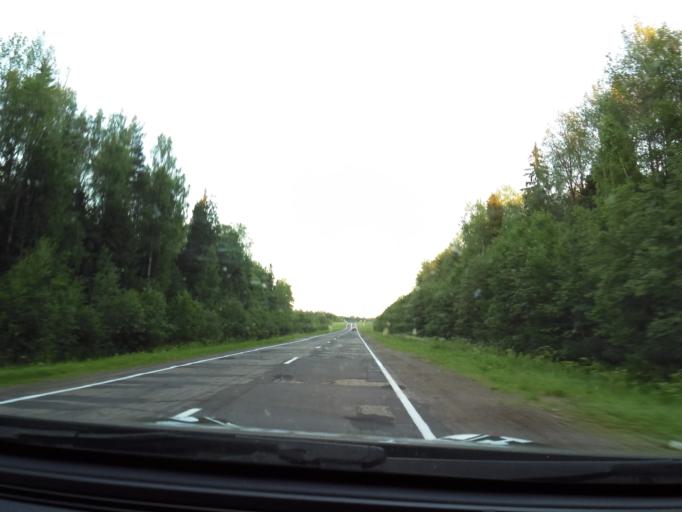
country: RU
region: Jaroslavl
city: Lyubim
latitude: 58.3564
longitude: 40.6099
